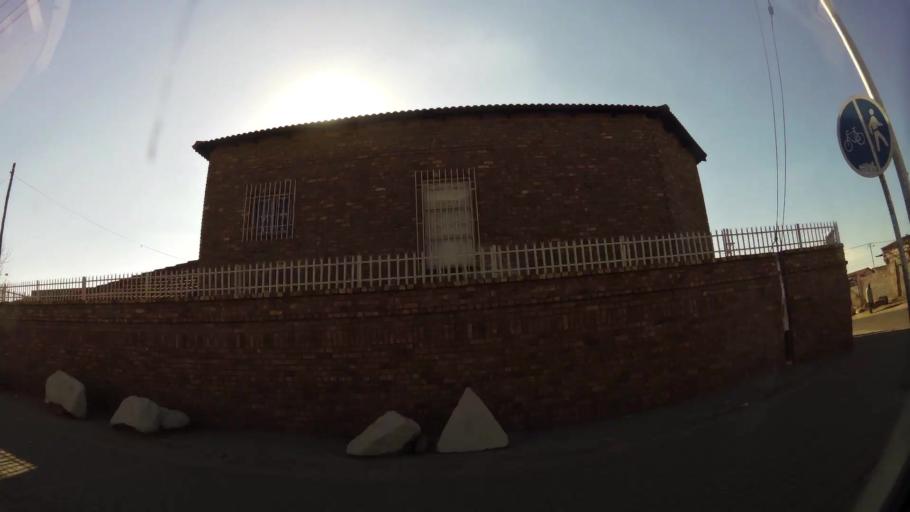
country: ZA
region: Gauteng
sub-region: City of Tshwane Metropolitan Municipality
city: Cullinan
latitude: -25.7131
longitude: 28.3839
